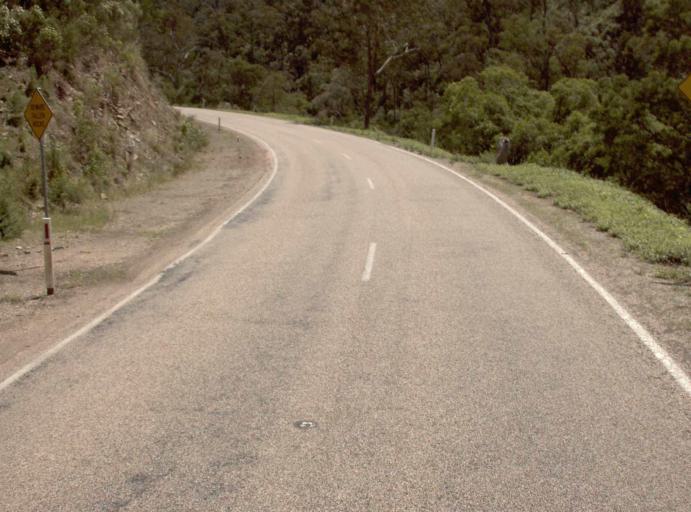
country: AU
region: Victoria
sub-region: East Gippsland
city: Lakes Entrance
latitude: -37.5302
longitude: 147.8534
